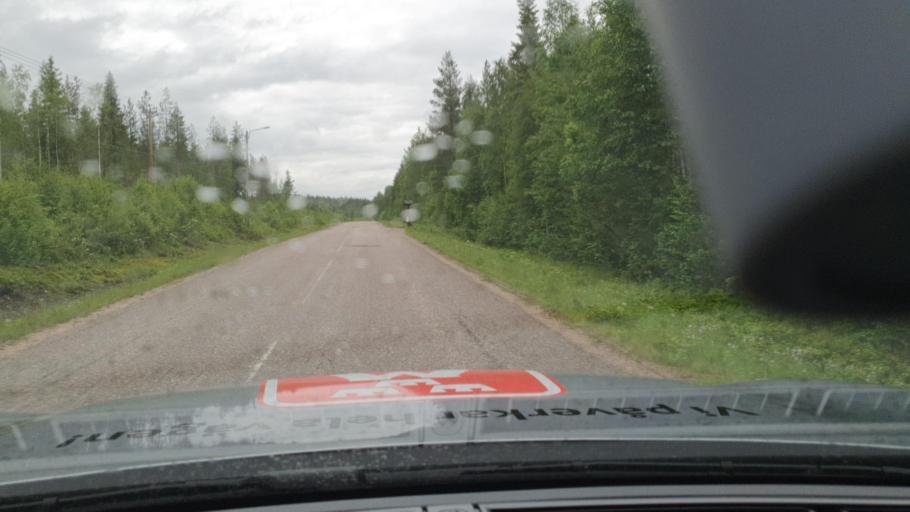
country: SE
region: Norrbotten
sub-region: Overkalix Kommun
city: OEverkalix
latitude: 66.3996
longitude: 22.7889
